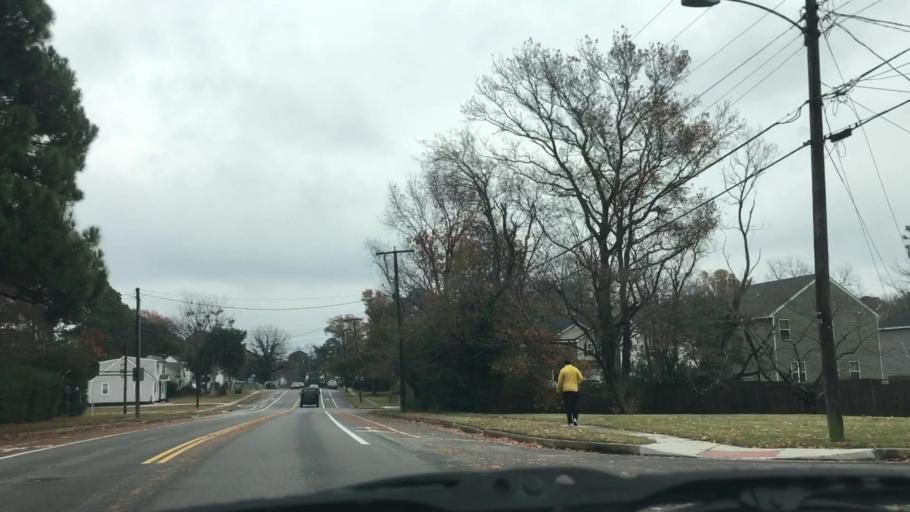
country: US
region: Virginia
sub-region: City of Norfolk
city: Norfolk
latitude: 36.8770
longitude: -76.2444
